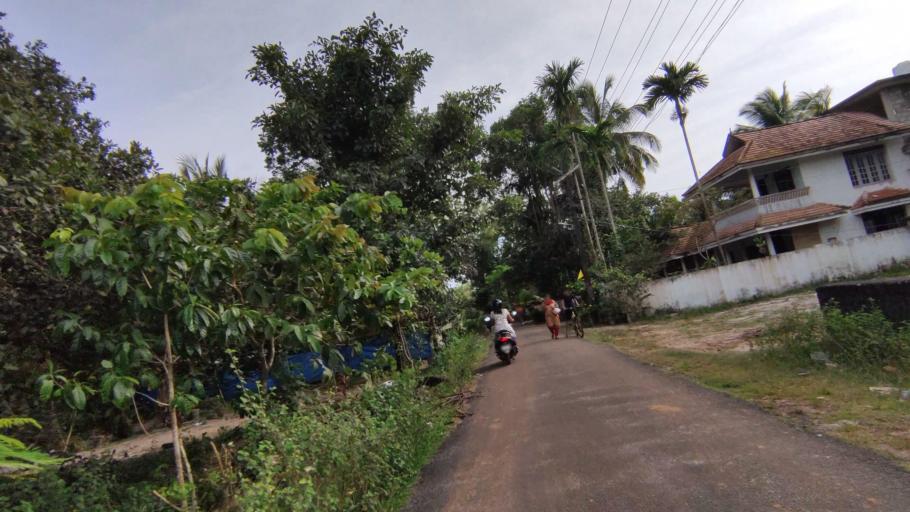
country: IN
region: Kerala
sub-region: Alappuzha
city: Shertallai
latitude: 9.6419
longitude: 76.3395
